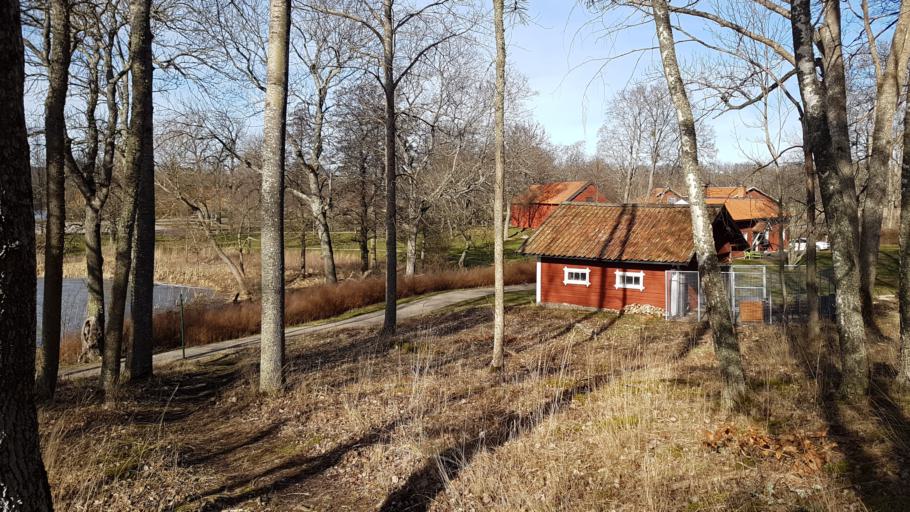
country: SE
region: Soedermanland
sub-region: Strangnas Kommun
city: Stallarholmen
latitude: 59.4713
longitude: 17.2477
